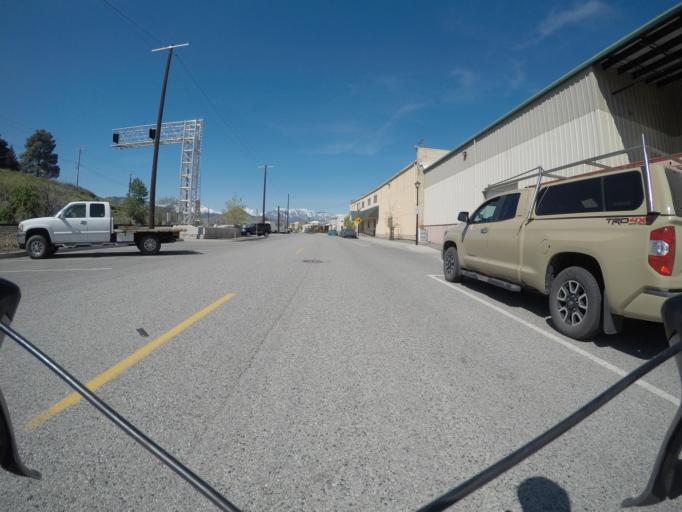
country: US
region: Washington
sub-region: Chelan County
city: Cashmere
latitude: 47.5203
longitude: -120.4641
